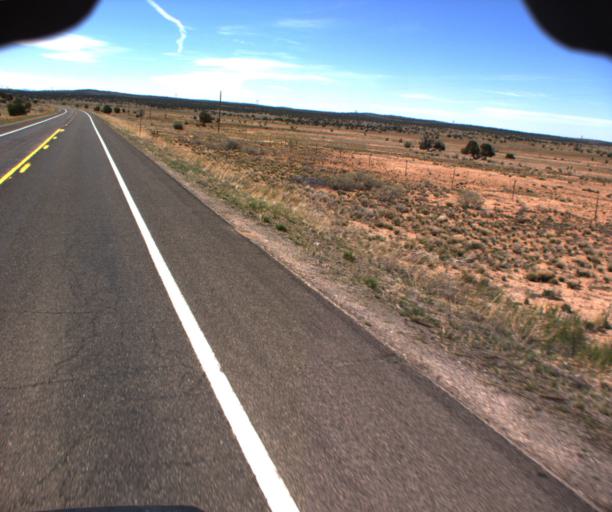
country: US
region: Arizona
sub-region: Mohave County
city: Peach Springs
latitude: 35.5524
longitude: -113.3137
